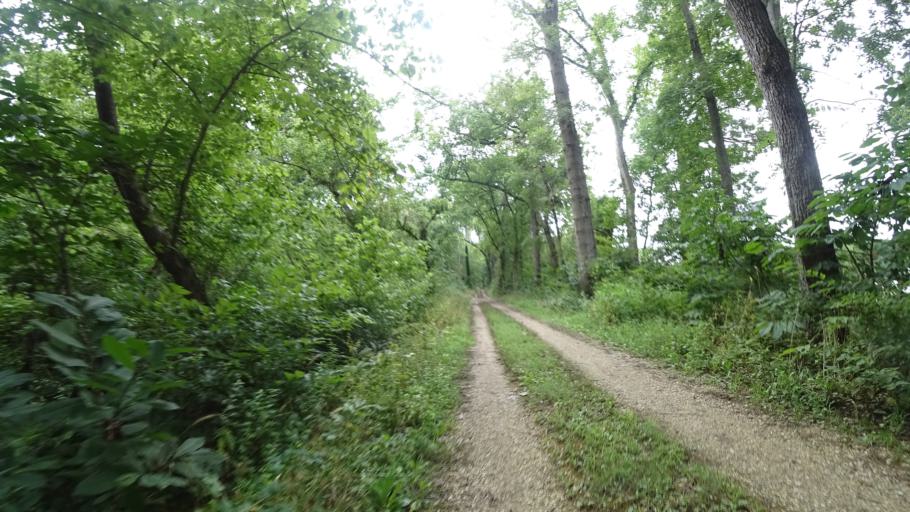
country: US
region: Virginia
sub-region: Loudoun County
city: Lowes Island
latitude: 39.0676
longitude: -77.3814
